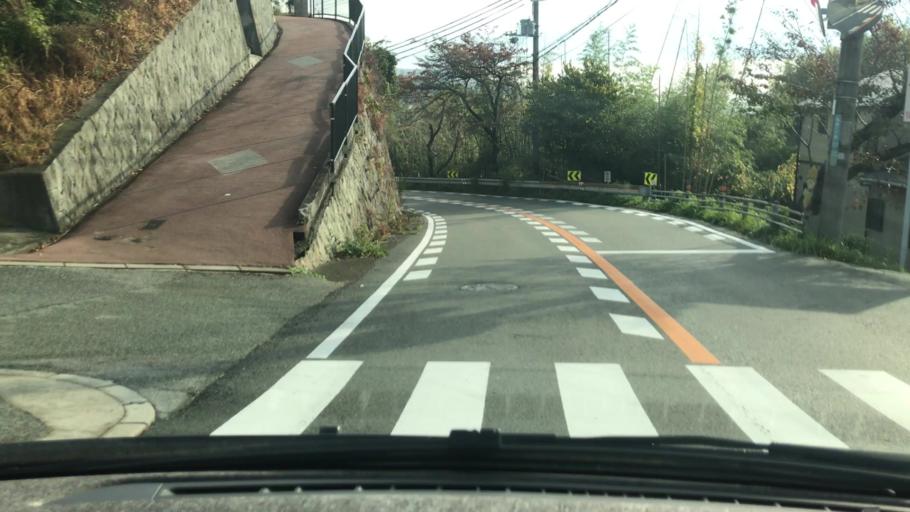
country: JP
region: Hyogo
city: Takarazuka
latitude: 34.8303
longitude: 135.2945
